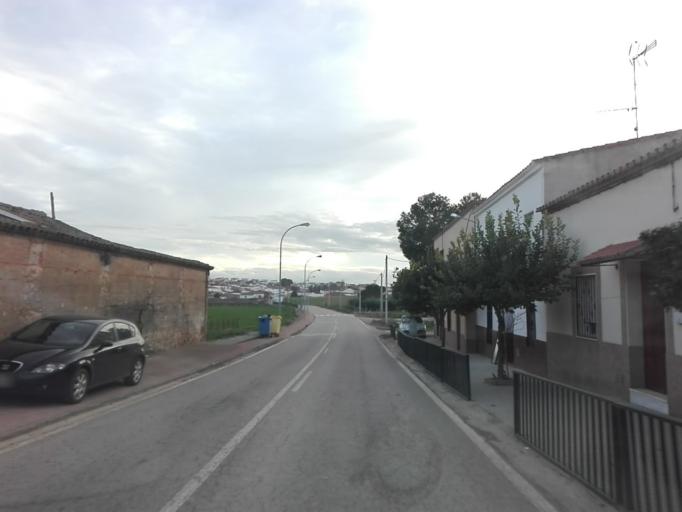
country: ES
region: Extremadura
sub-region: Provincia de Badajoz
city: Usagre
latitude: 38.3641
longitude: -6.1642
